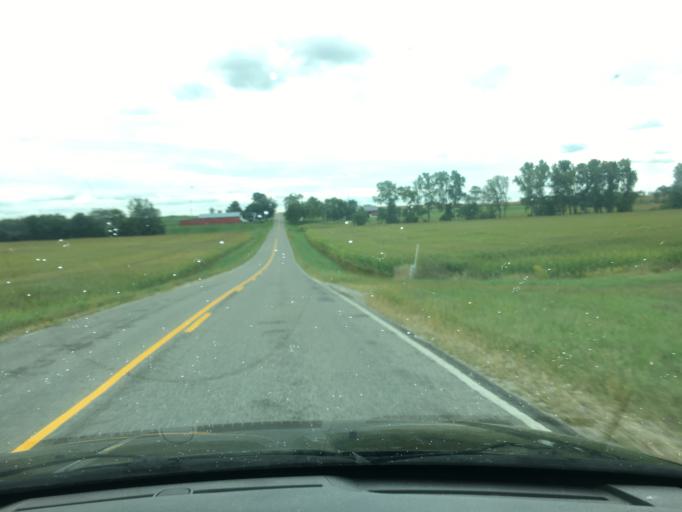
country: US
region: Ohio
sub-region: Champaign County
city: Urbana
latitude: 40.1721
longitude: -83.6889
